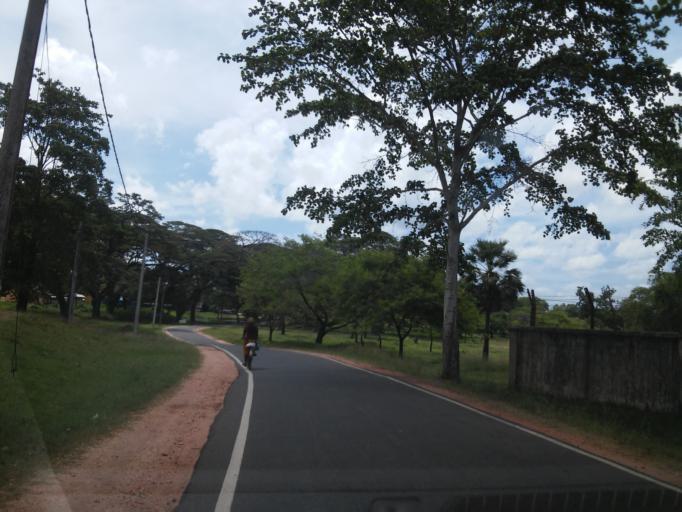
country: LK
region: North Central
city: Anuradhapura
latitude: 8.3487
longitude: 80.3993
